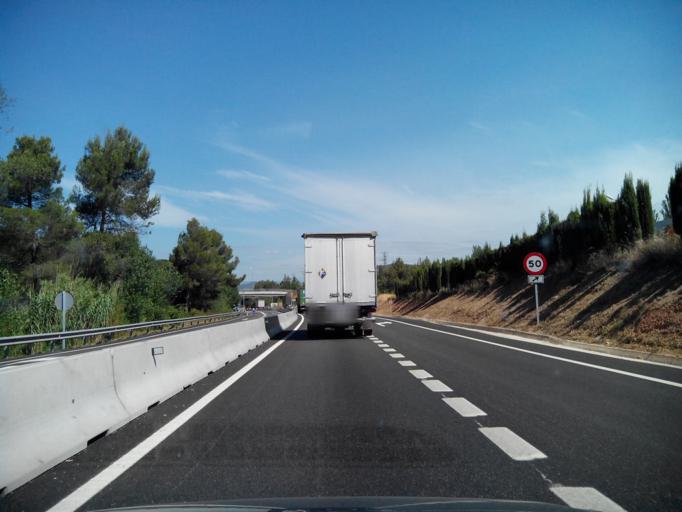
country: ES
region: Catalonia
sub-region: Provincia de Barcelona
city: Monistrol de Montserrat
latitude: 41.5950
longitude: 1.8966
